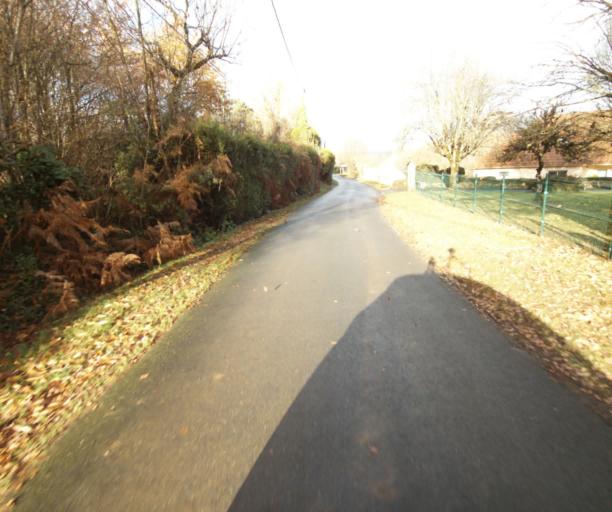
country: FR
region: Limousin
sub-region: Departement de la Correze
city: Saint-Mexant
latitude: 45.2564
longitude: 1.6241
